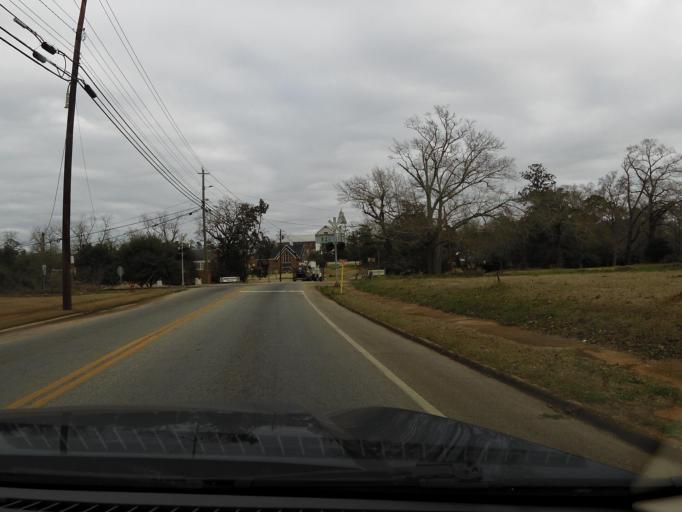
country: US
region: Georgia
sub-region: Randolph County
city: Cuthbert
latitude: 31.7716
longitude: -84.7982
